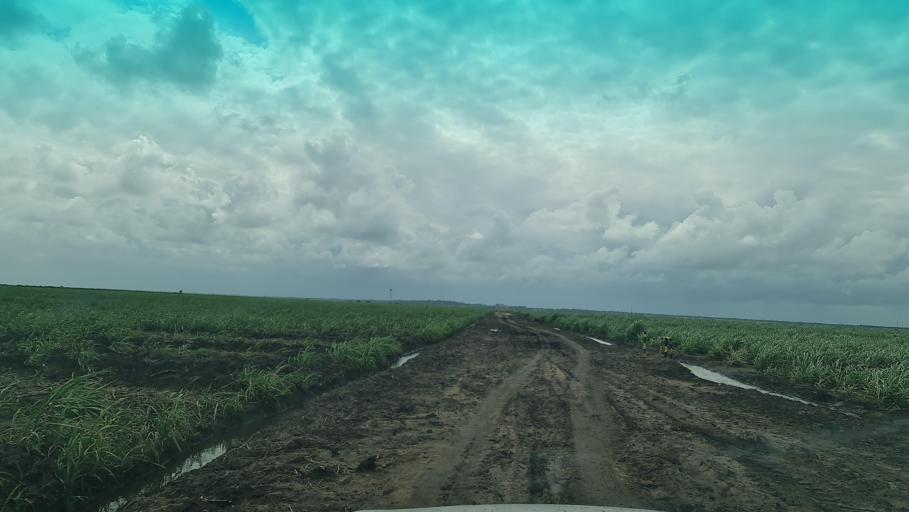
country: MZ
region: Maputo
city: Manhica
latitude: -25.4538
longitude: 32.8366
